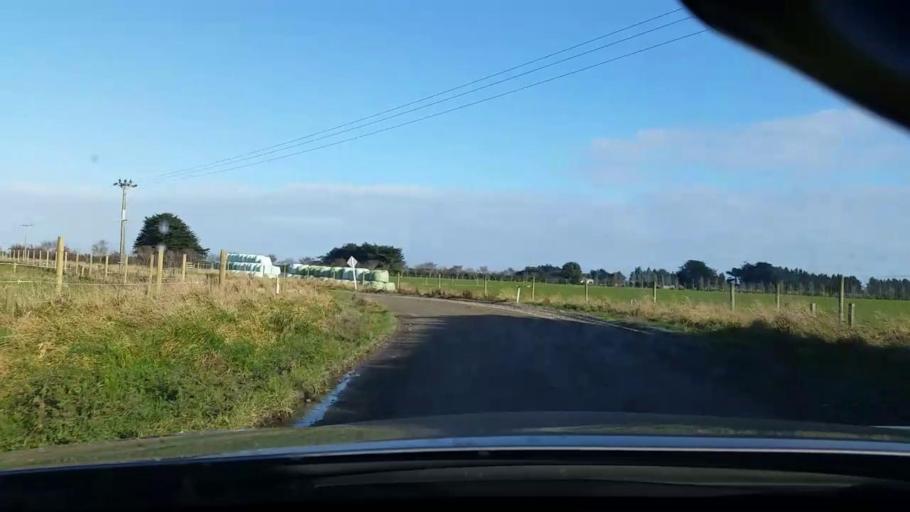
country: NZ
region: Southland
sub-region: Invercargill City
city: Invercargill
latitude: -46.2989
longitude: 168.3037
